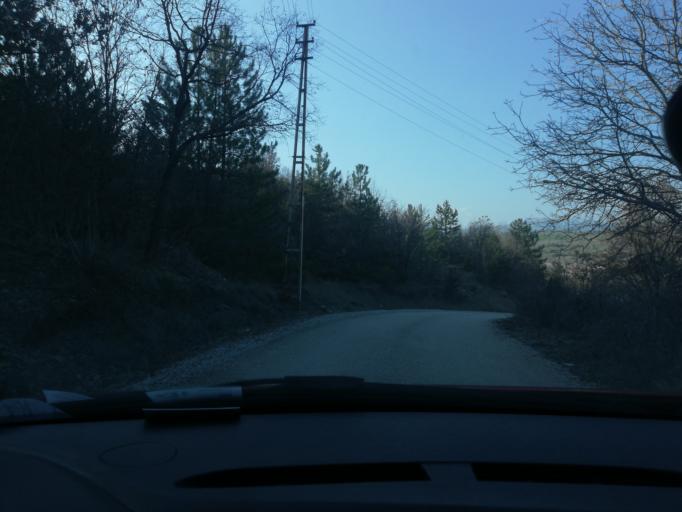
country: TR
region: Karabuk
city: Safranbolu
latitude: 41.2138
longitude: 32.7465
